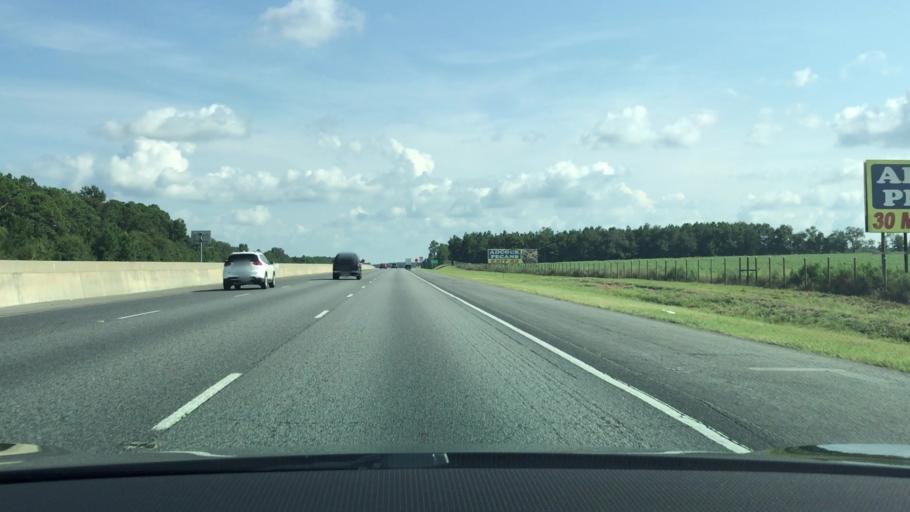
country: US
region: Georgia
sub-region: Turner County
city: Ashburn
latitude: 31.8275
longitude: -83.7122
